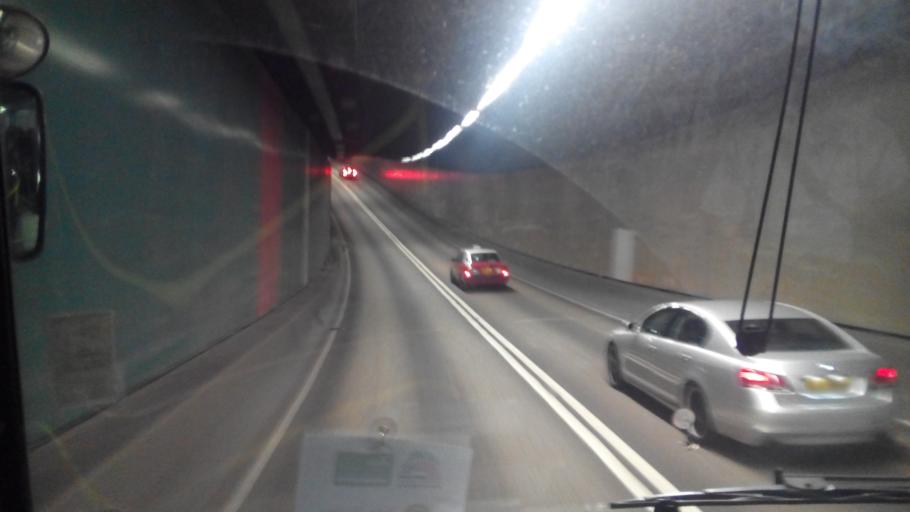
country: HK
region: Central and Western
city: Central
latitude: 22.2832
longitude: 114.1583
